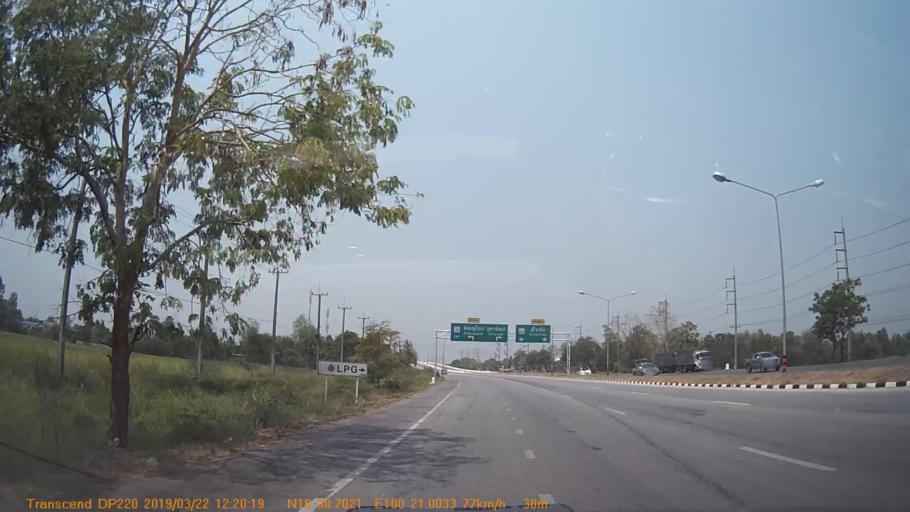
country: TH
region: Phitsanulok
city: Wang Thong
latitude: 16.8453
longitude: 100.3496
